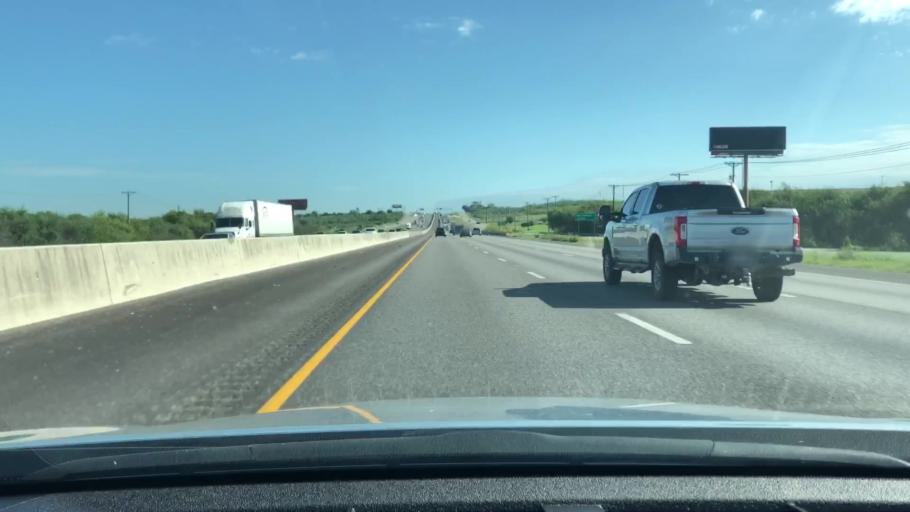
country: US
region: Texas
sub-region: Guadalupe County
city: Lake Dunlap
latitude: 29.7357
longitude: -98.0701
